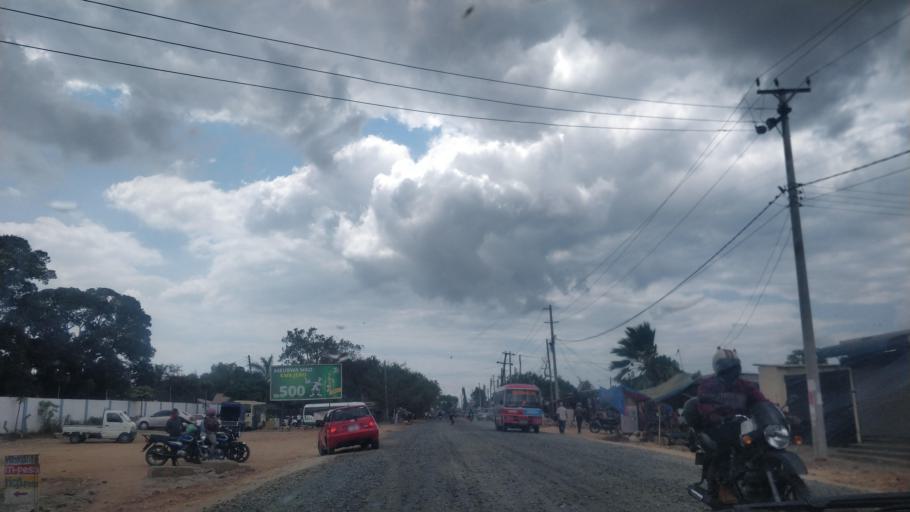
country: TZ
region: Dar es Salaam
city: Magomeni
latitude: -6.8067
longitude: 39.2231
